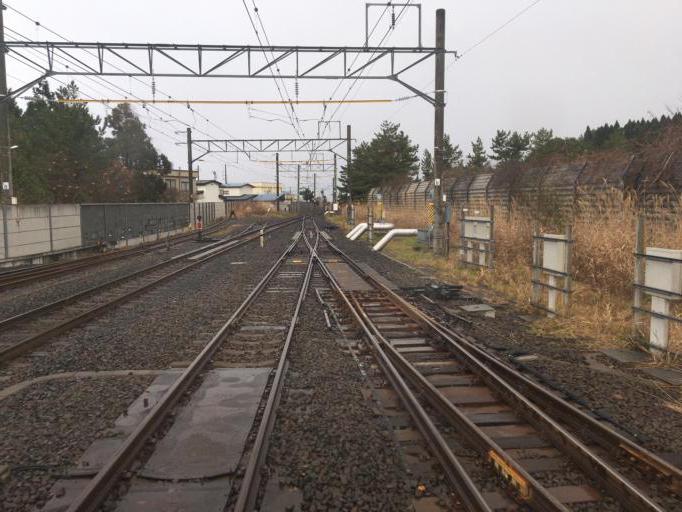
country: JP
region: Aomori
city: Aomori Shi
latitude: 41.0373
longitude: 140.6436
